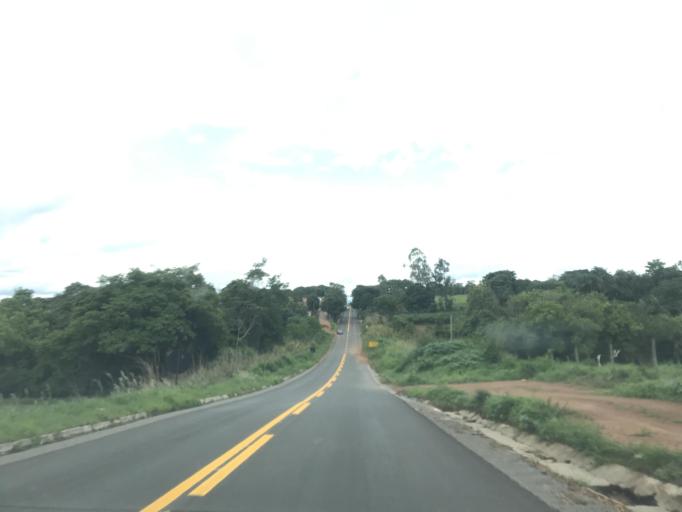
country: BR
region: Goias
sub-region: Bela Vista De Goias
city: Bela Vista de Goias
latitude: -17.0660
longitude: -48.6576
